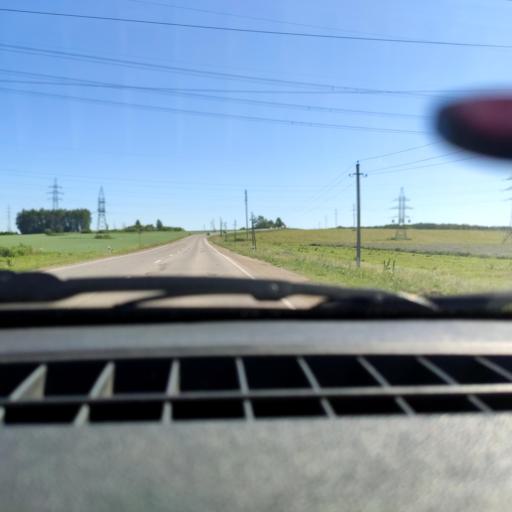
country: RU
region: Bashkortostan
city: Iglino
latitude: 54.9017
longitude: 56.4758
